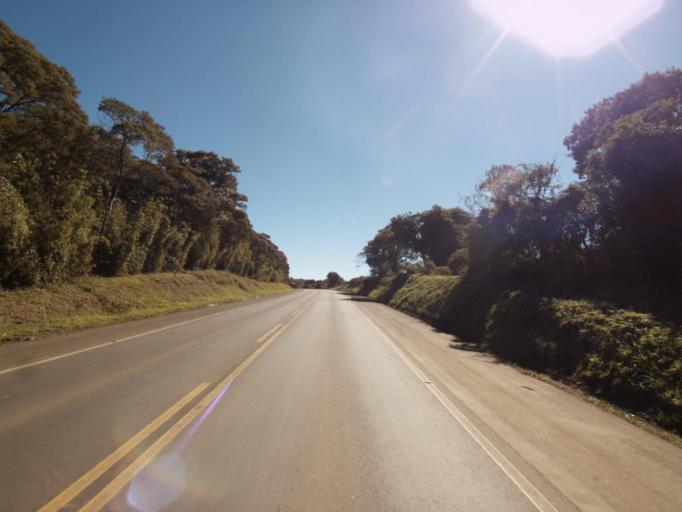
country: BR
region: Santa Catarina
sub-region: Xanxere
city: Xanxere
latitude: -26.8711
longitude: -52.1977
